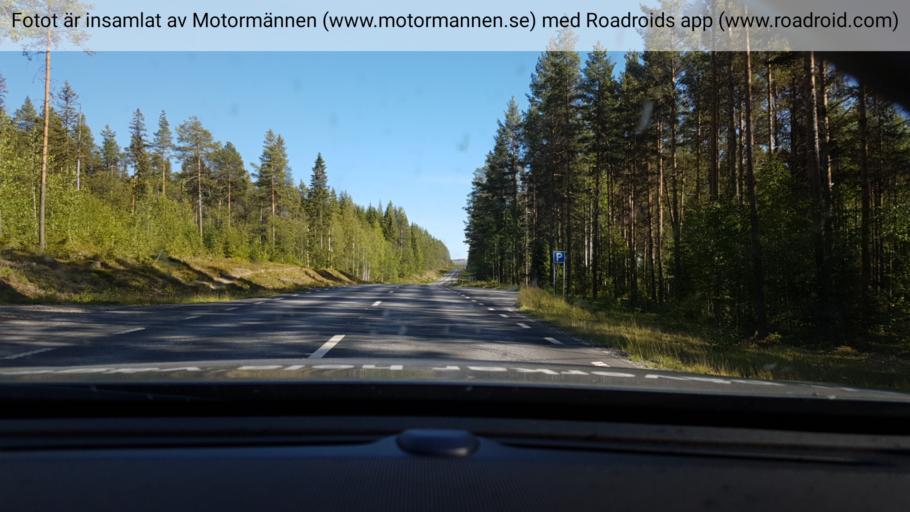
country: SE
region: Vaesterbotten
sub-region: Lycksele Kommun
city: Lycksele
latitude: 64.5460
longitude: 18.7440
